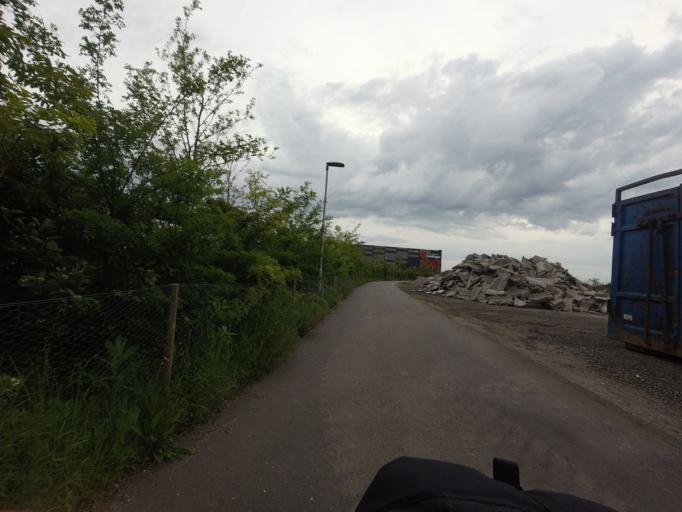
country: SE
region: Skane
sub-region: Malmo
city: Malmoe
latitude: 55.6312
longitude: 13.0085
